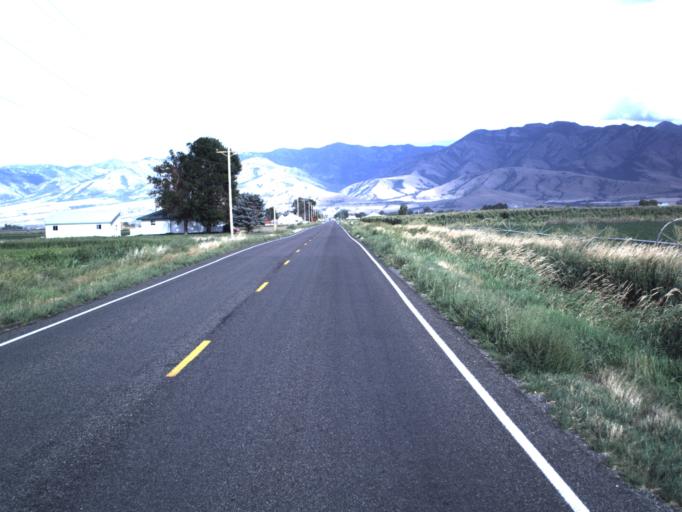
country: US
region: Utah
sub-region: Cache County
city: Lewiston
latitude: 41.9756
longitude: -111.8924
